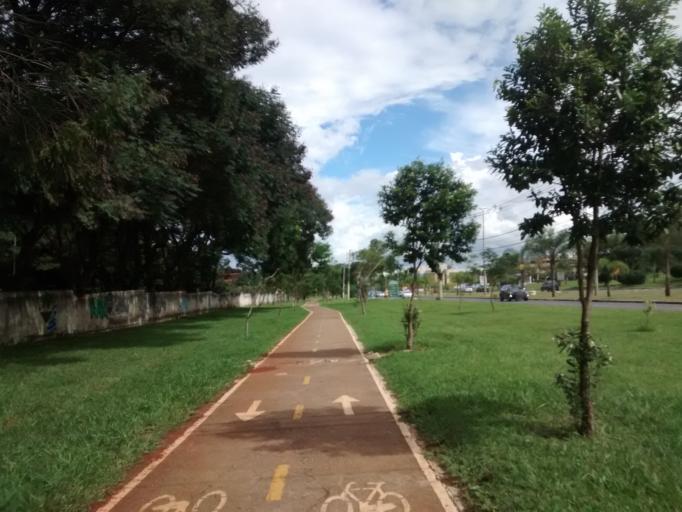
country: BR
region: Federal District
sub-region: Brasilia
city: Brasilia
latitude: -15.7914
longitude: -47.9158
